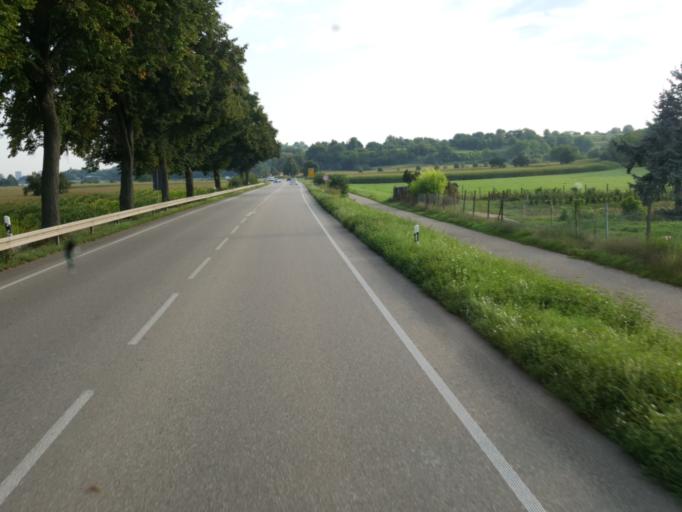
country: DE
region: Baden-Wuerttemberg
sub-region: Freiburg Region
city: Kippenheim
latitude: 48.3060
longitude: 7.8318
